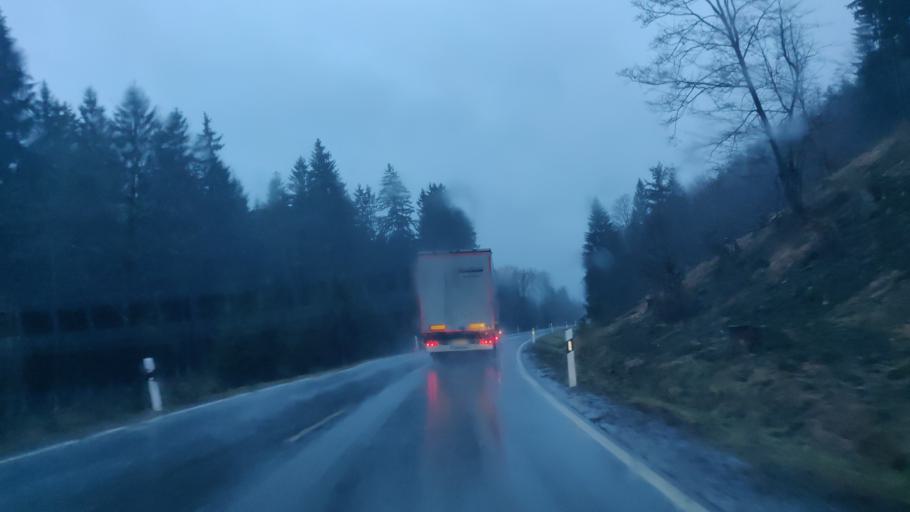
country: DE
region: Lower Saxony
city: Wieda
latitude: 51.6783
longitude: 10.5676
